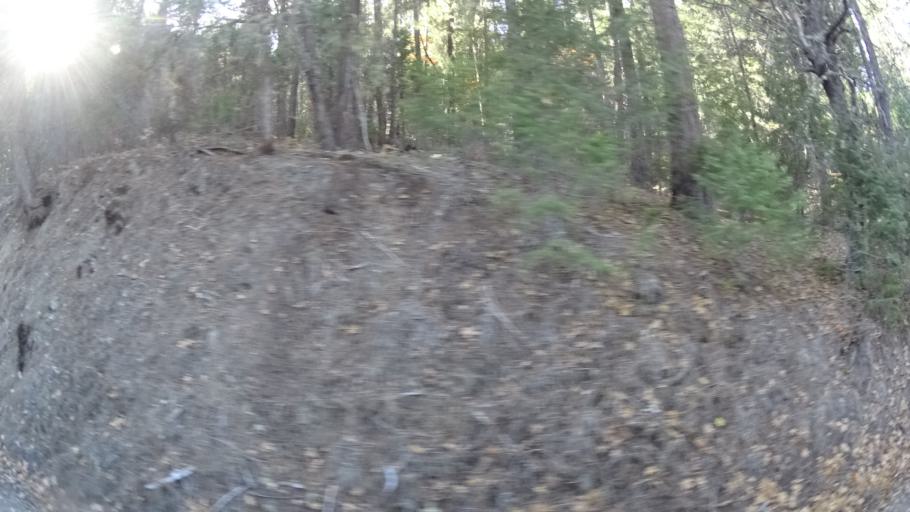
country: US
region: California
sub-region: Siskiyou County
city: Yreka
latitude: 41.8418
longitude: -122.8829
